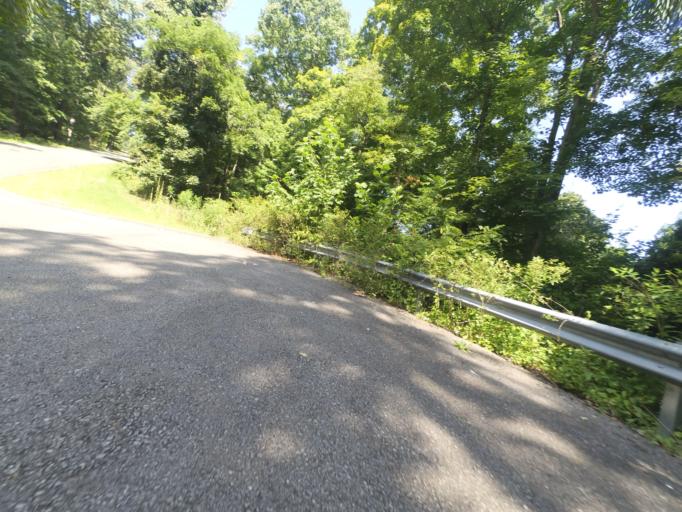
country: US
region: West Virginia
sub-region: Cabell County
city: Huntington
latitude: 38.3821
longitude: -82.4600
